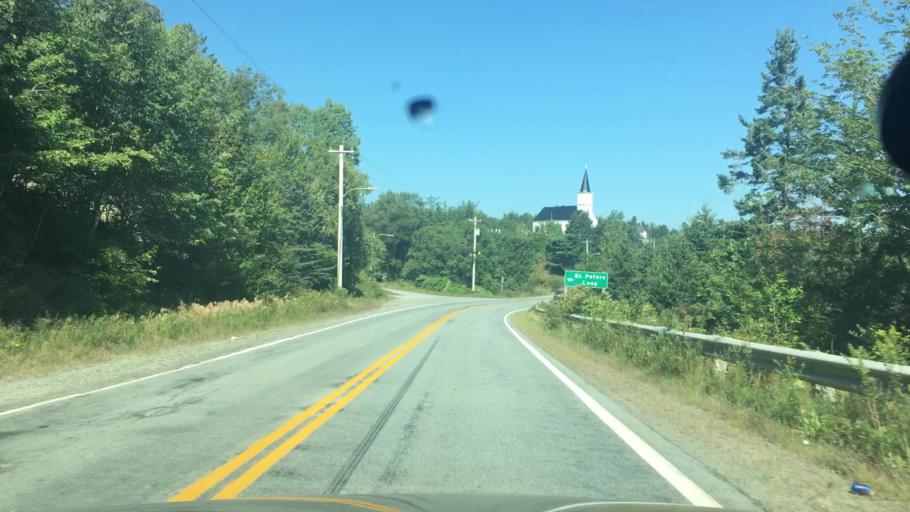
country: CA
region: Nova Scotia
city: New Glasgow
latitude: 44.9216
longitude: -62.5446
